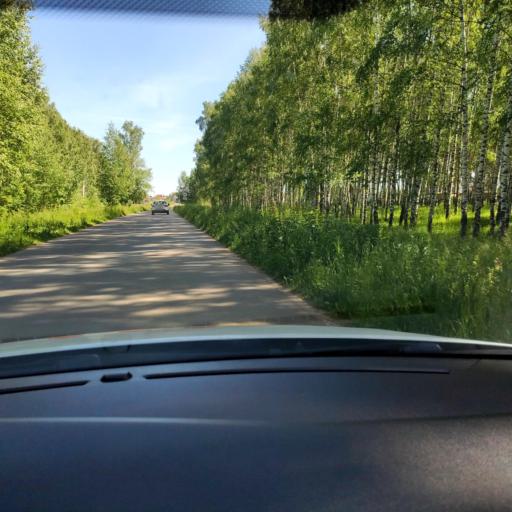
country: RU
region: Tatarstan
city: Staroye Arakchino
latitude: 55.8886
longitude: 49.0343
